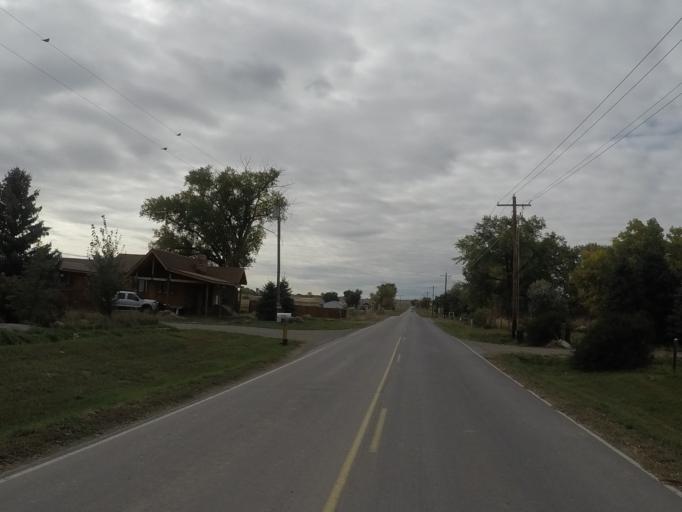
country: US
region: Montana
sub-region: Yellowstone County
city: Laurel
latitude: 45.7697
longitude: -108.6609
